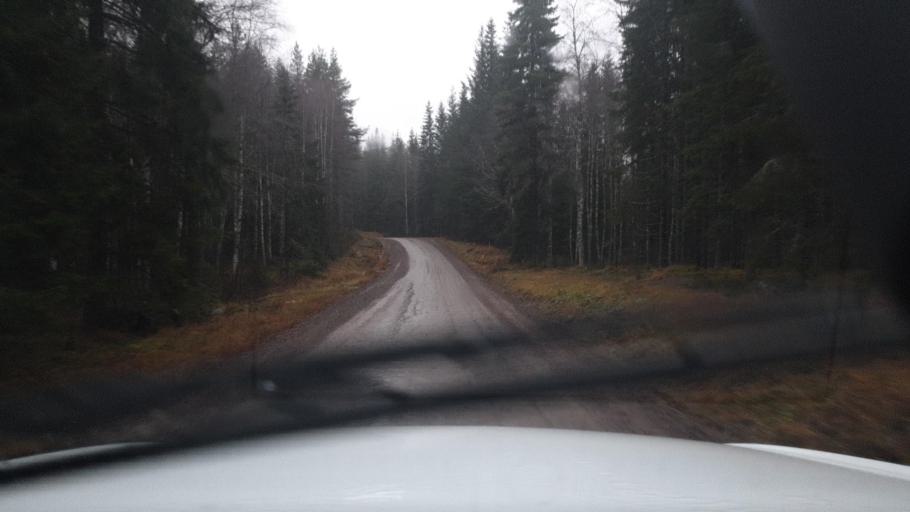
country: SE
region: Vaermland
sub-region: Arvika Kommun
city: Arvika
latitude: 59.9927
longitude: 12.6618
